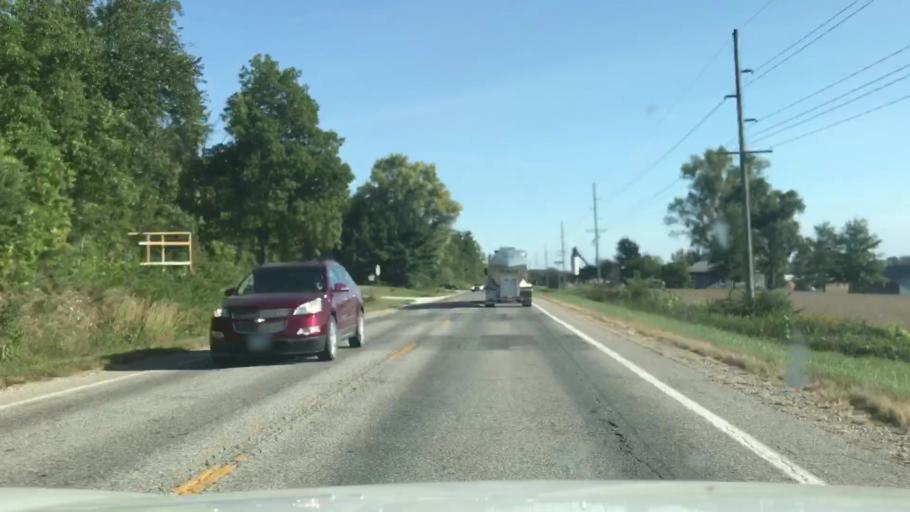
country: US
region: Illinois
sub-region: Adams County
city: Quincy
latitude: 39.8530
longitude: -91.3820
